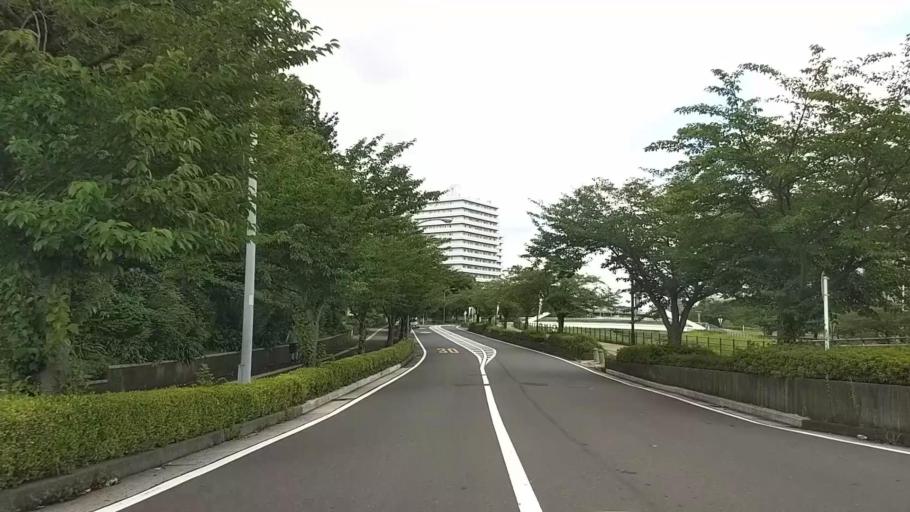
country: JP
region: Kanagawa
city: Yokohama
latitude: 35.5098
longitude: 139.6111
